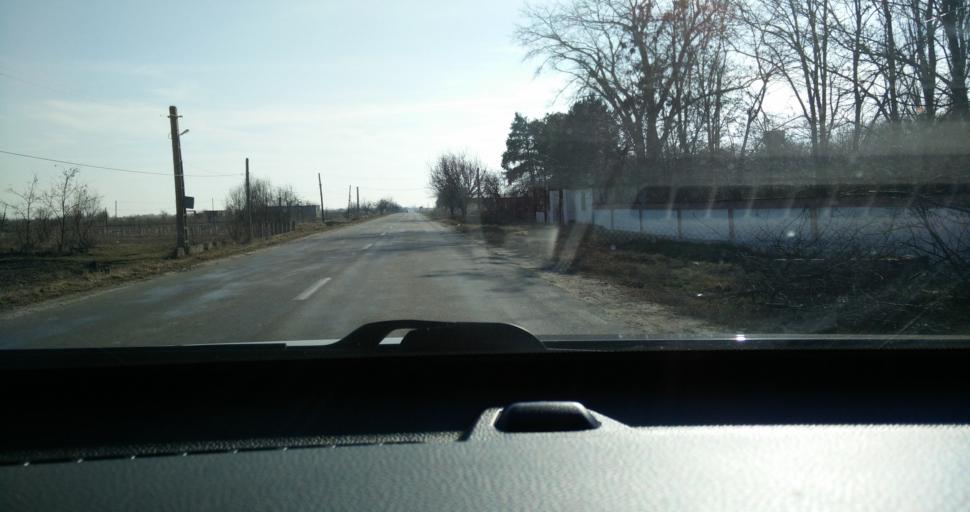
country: RO
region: Vrancea
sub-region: Comuna Nanesti
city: Nanesti
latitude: 45.5275
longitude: 27.4949
